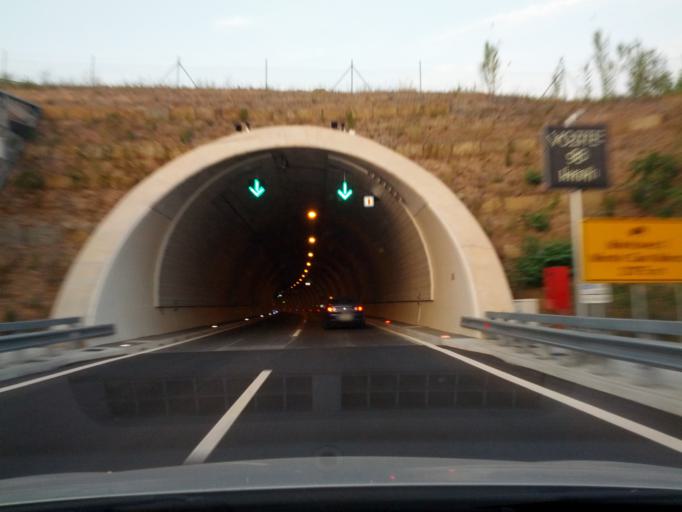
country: SI
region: Izola-Isola
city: Izola
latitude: 45.5391
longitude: 13.6888
